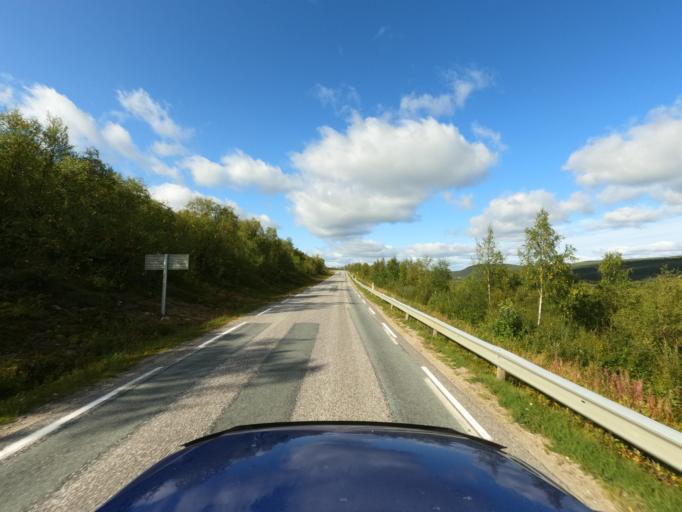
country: NO
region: Finnmark Fylke
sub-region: Karasjok
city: Karasjohka
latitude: 69.4367
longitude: 25.6677
